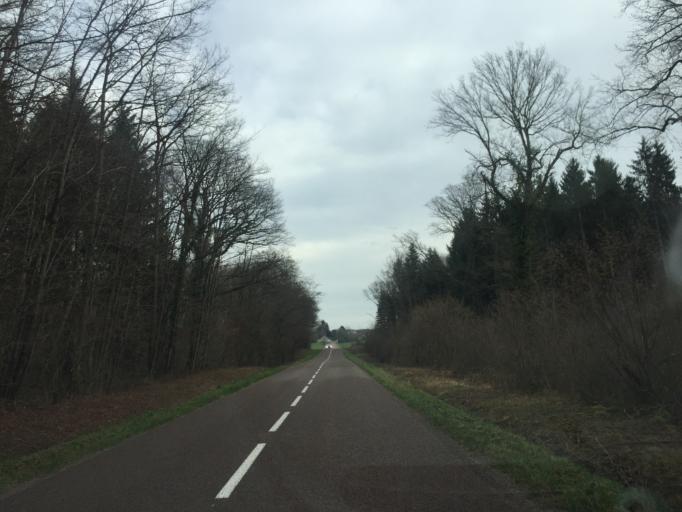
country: FR
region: Franche-Comte
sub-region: Departement du Jura
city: Chaussin
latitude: 46.9219
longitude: 5.5014
